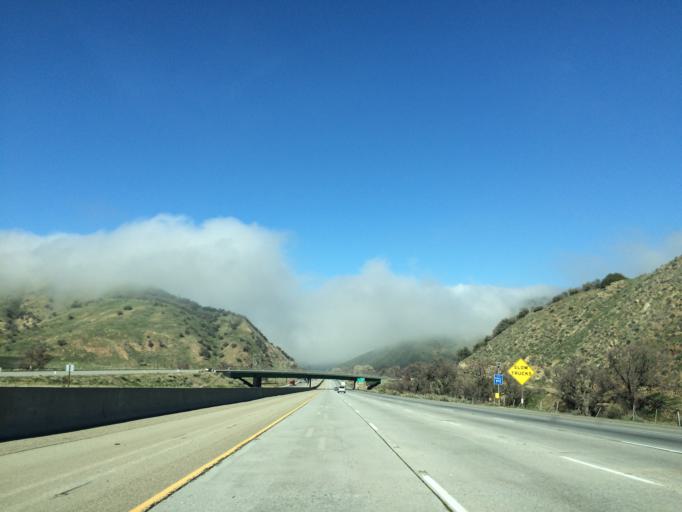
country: US
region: California
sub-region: Kern County
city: Lebec
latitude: 34.8637
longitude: -118.8809
